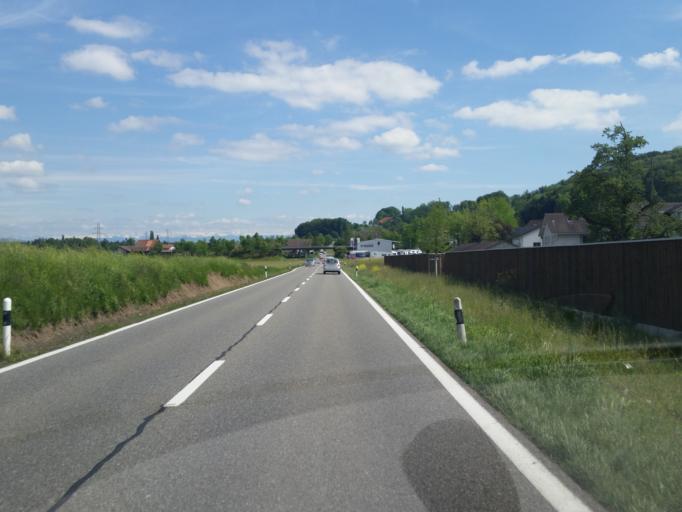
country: CH
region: Aargau
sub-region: Bezirk Bremgarten
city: Wohlen
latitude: 47.3334
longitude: 8.2812
